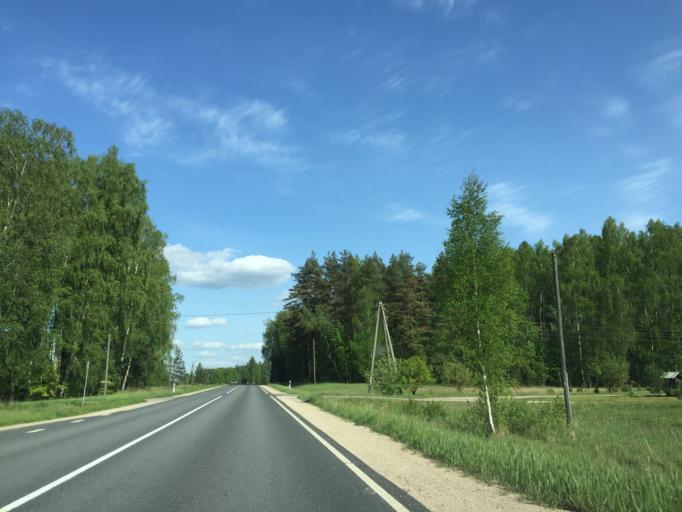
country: LV
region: Salaspils
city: Salaspils
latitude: 56.8227
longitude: 24.3907
